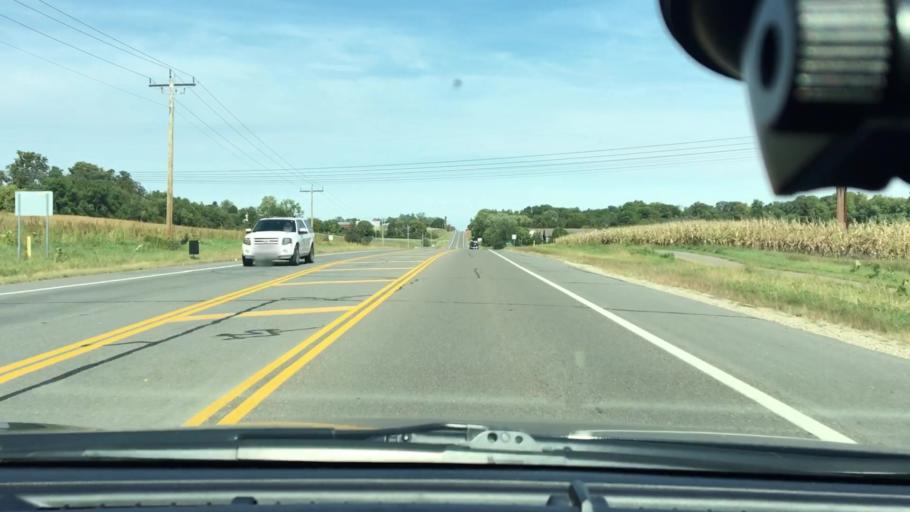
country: US
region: Minnesota
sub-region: Wright County
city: Hanover
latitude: 45.1752
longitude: -93.6656
